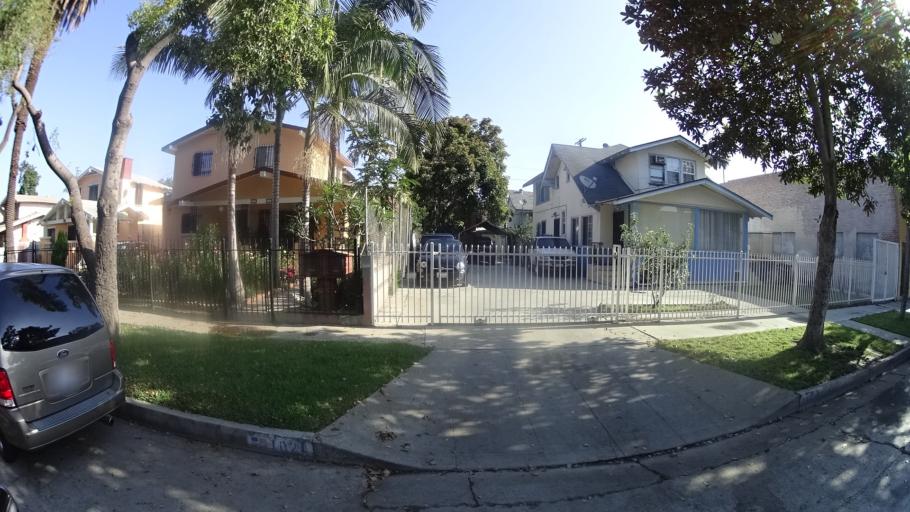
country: US
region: California
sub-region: Los Angeles County
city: Westmont
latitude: 33.9754
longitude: -118.2925
